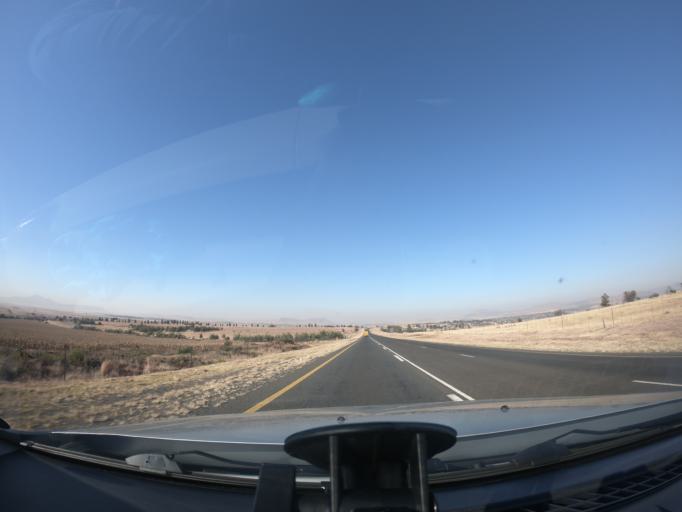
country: ZA
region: Mpumalanga
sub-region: Gert Sibande District Municipality
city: Volksrust
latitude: -27.3292
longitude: 29.8921
